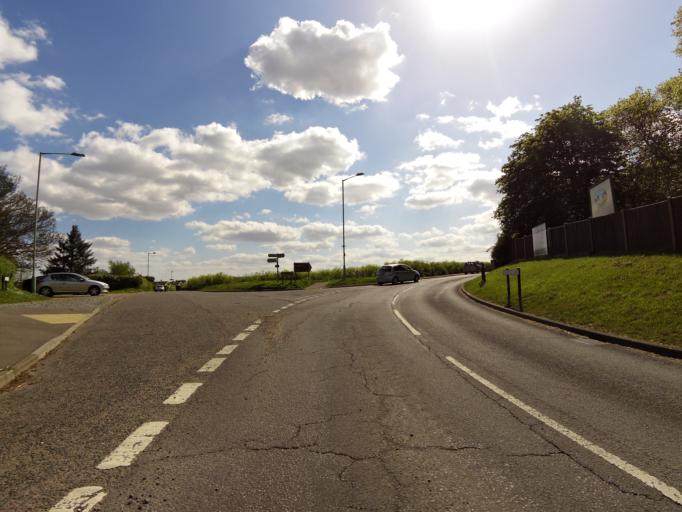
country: GB
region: England
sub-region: Suffolk
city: Kessingland
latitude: 52.4516
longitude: 1.6923
